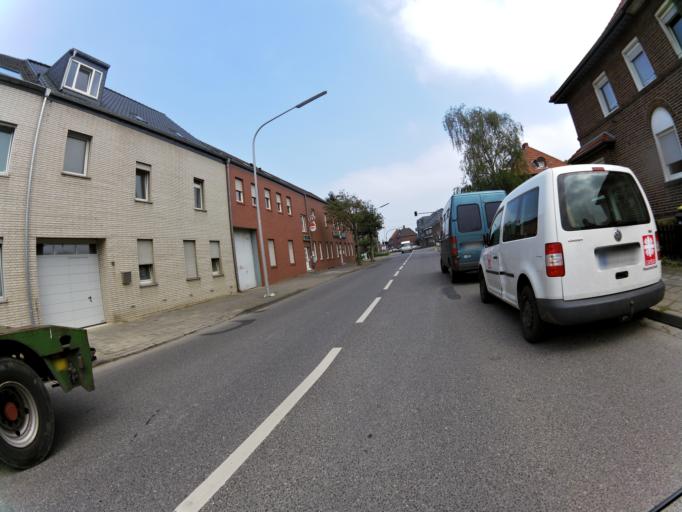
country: DE
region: North Rhine-Westphalia
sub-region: Regierungsbezirk Koln
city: Heinsberg
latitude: 51.0452
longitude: 6.1512
